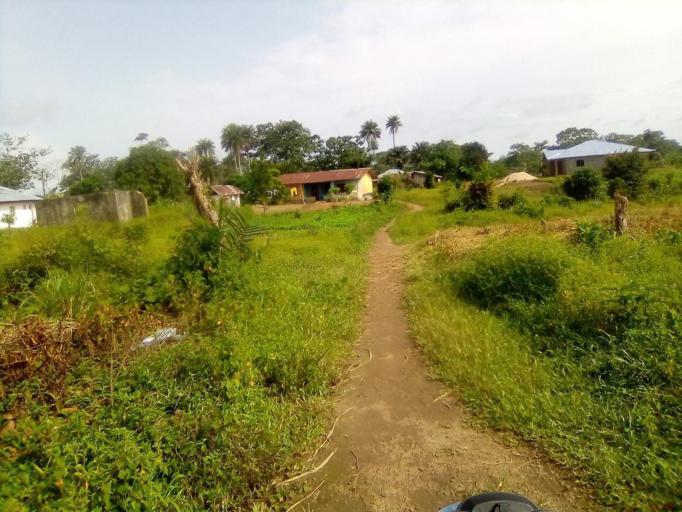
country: SL
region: Southern Province
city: Pujehun
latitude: 7.3646
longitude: -11.7280
